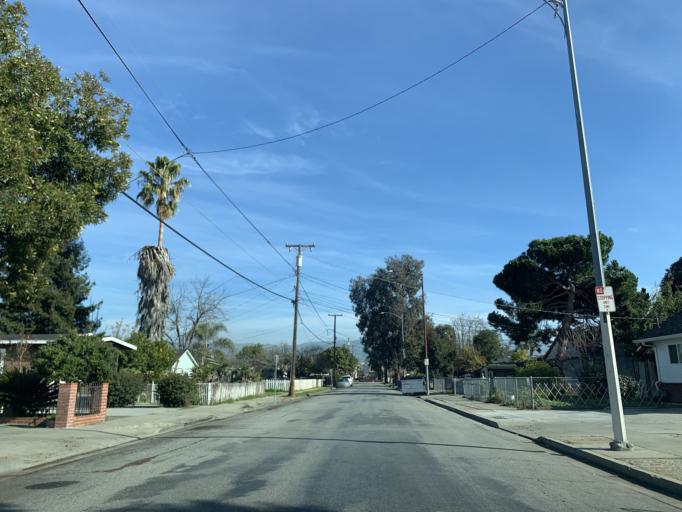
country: US
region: California
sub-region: Santa Clara County
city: San Jose
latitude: 37.3426
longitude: -121.8603
